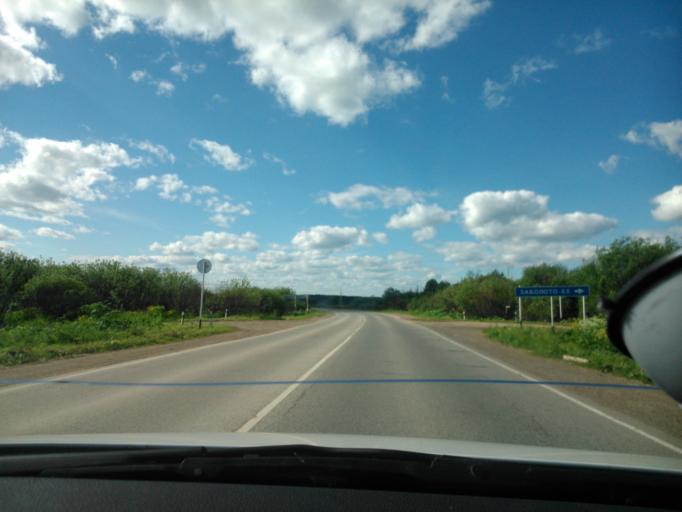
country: RU
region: Perm
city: Ust'-Kachka
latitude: 57.9377
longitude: 55.7578
